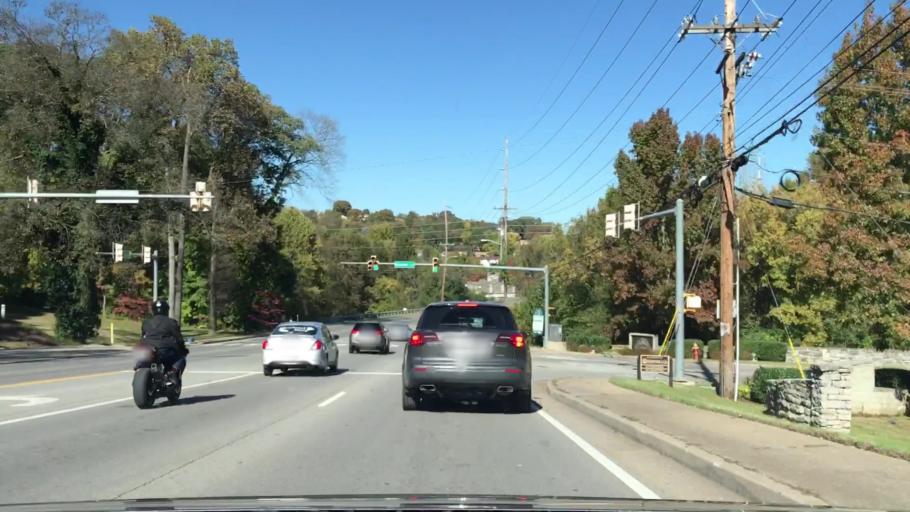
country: US
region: Tennessee
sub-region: Williamson County
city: Brentwood Estates
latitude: 36.0419
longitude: -86.7264
